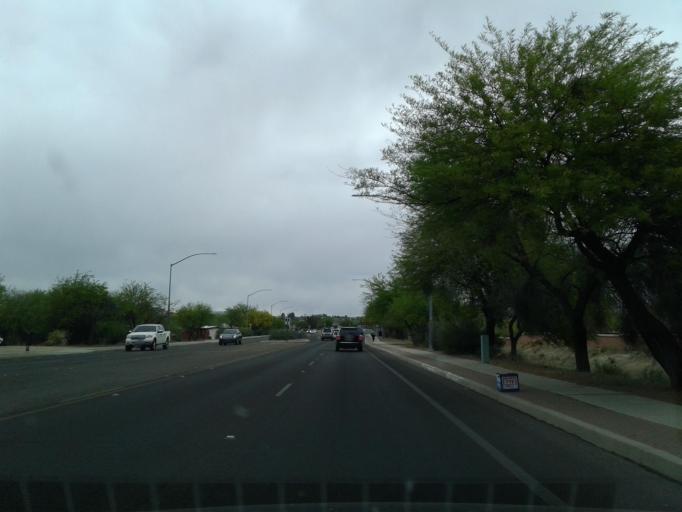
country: US
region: Arizona
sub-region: Pima County
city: Flowing Wells
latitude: 32.2835
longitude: -110.9695
